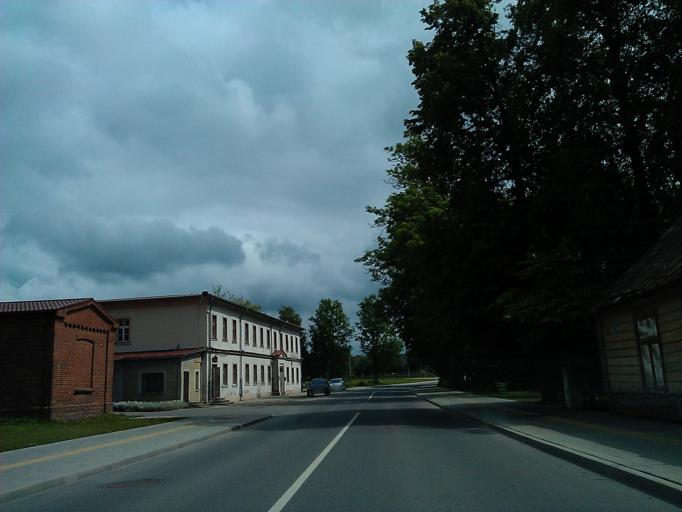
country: LV
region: Aizpute
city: Aizpute
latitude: 56.7162
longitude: 21.6135
